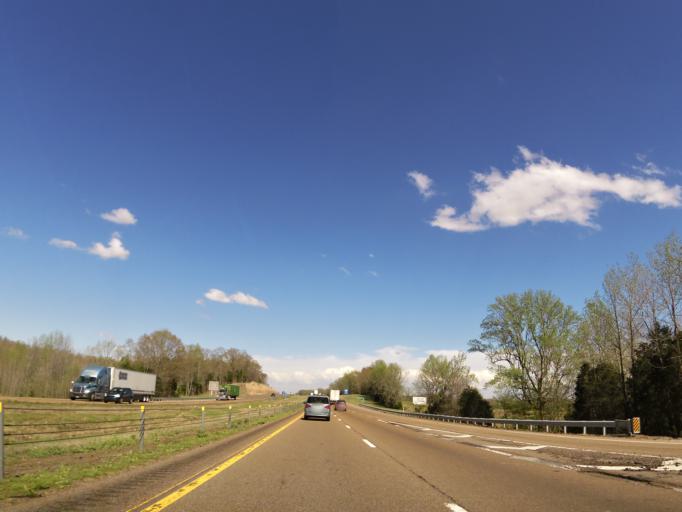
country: US
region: Tennessee
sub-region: Henderson County
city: Lexington
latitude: 35.7549
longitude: -88.5108
